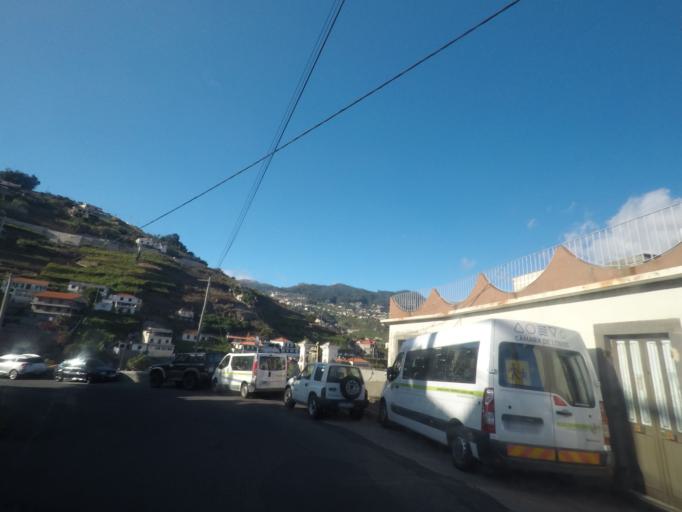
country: PT
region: Madeira
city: Camara de Lobos
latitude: 32.6649
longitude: -16.9904
